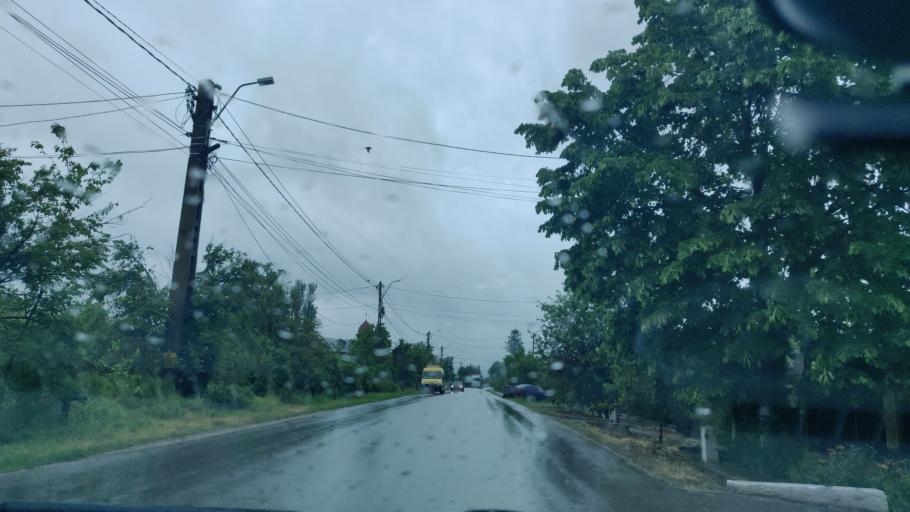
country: RO
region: Giurgiu
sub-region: Comuna Bulbucata
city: Bulbucata
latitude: 44.2810
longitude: 25.8126
